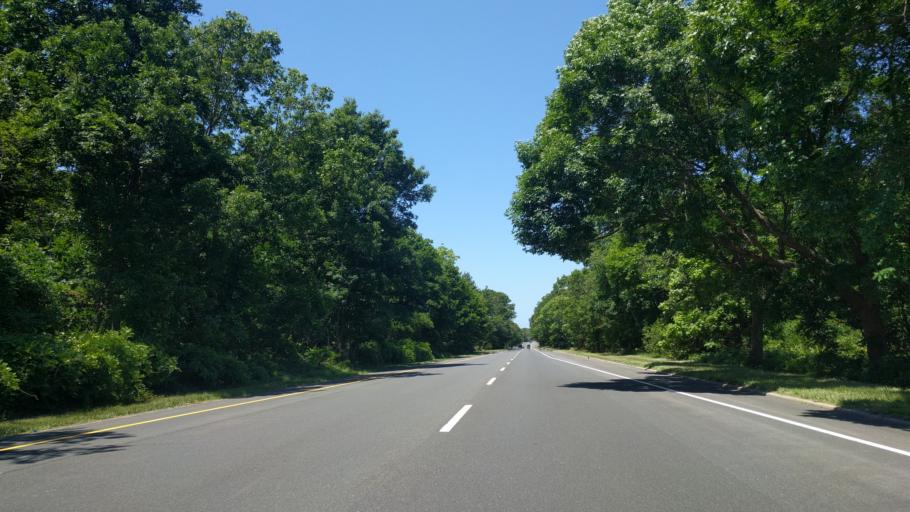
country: US
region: New York
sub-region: Suffolk County
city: Manorville
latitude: 40.8620
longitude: -72.7696
